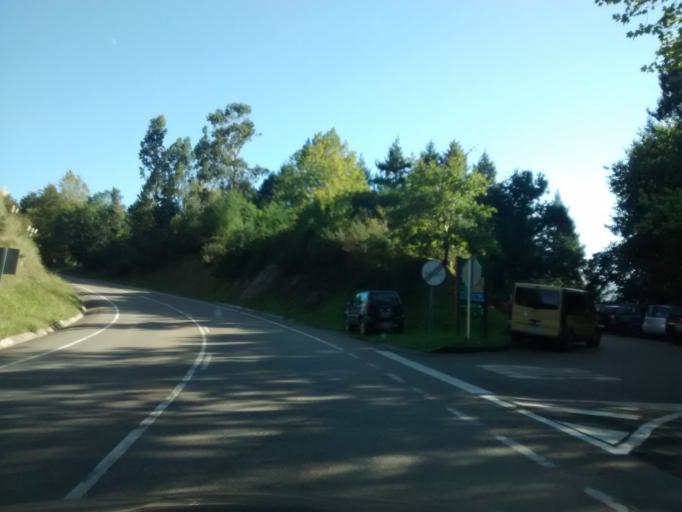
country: ES
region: Cantabria
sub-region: Provincia de Cantabria
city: Cabezon de la Sal
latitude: 43.3211
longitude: -4.2577
